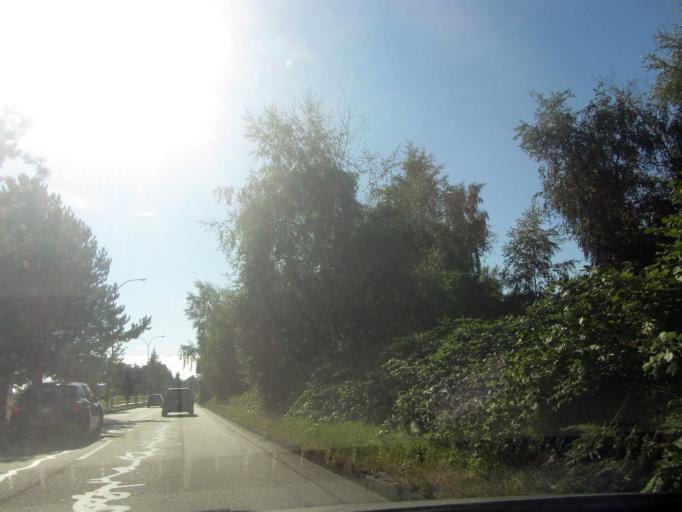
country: CA
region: British Columbia
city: Richmond
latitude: 49.1774
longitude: -123.1172
